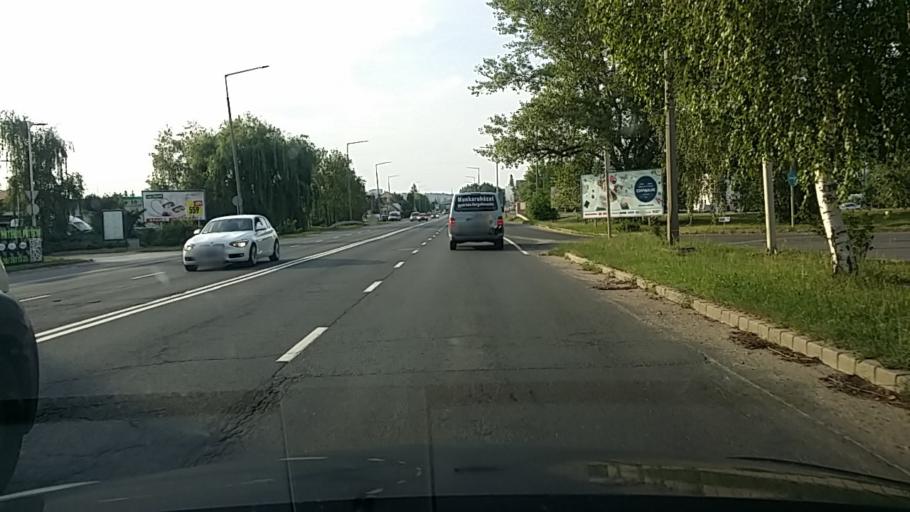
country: HU
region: Borsod-Abauj-Zemplen
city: Miskolc
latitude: 48.0565
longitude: 20.7976
